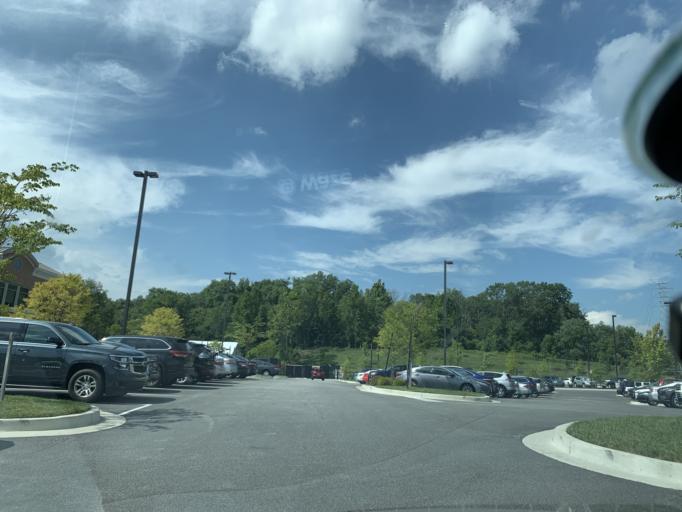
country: US
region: Maryland
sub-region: Baltimore County
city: Mays Chapel
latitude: 39.4222
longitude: -76.6681
